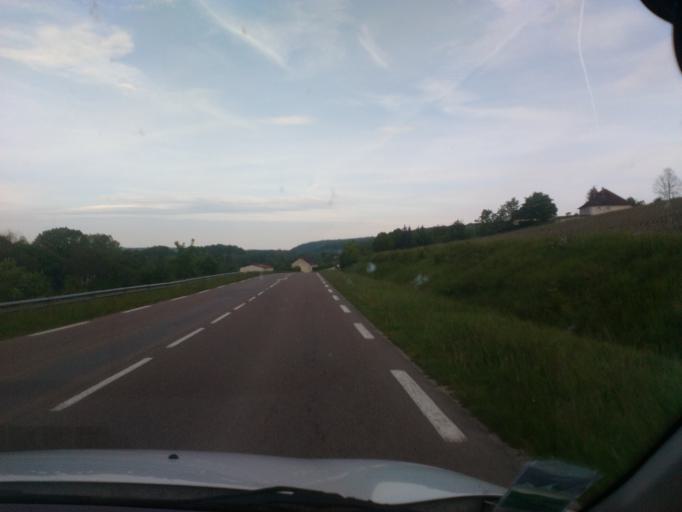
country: FR
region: Champagne-Ardenne
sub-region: Departement de l'Aube
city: Bar-sur-Aube
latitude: 48.2646
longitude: 4.6587
